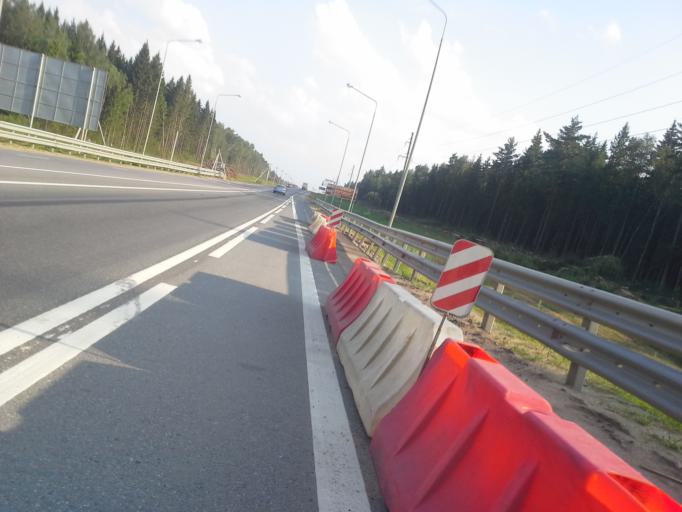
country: RU
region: Moskovskaya
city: Yershovo
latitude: 55.8176
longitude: 36.9176
